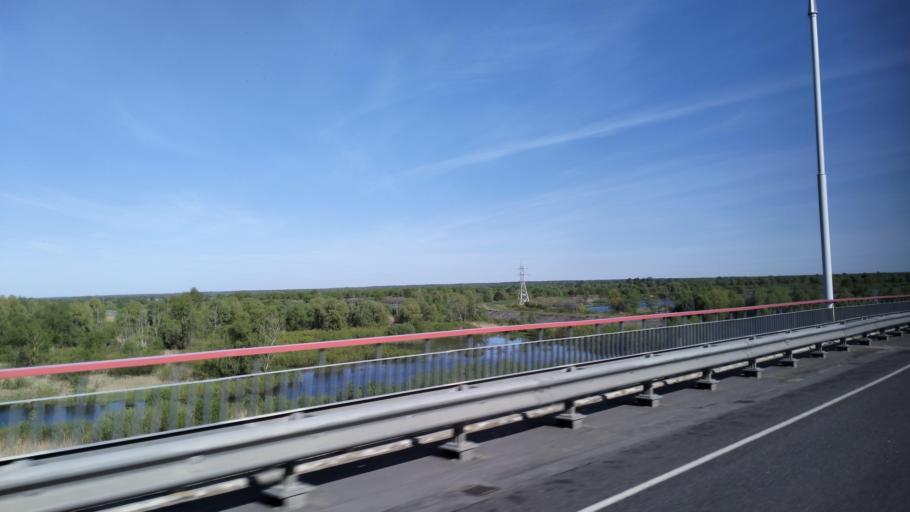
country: BY
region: Gomel
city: Turaw
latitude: 52.0815
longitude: 27.8263
